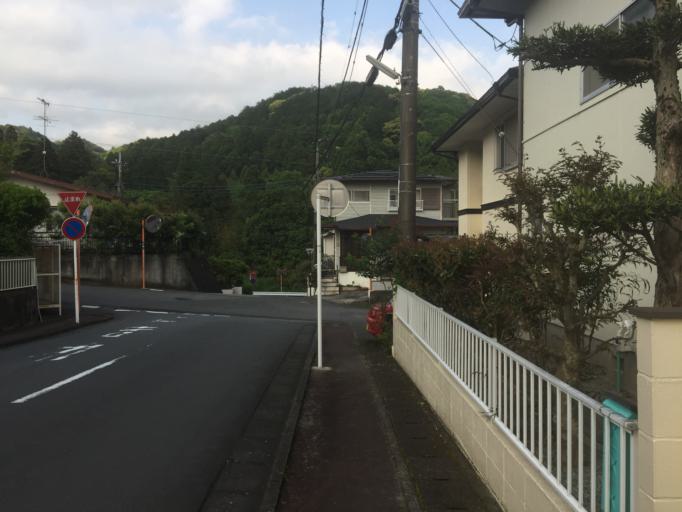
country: JP
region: Shizuoka
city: Mishima
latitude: 35.1799
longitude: 138.9347
